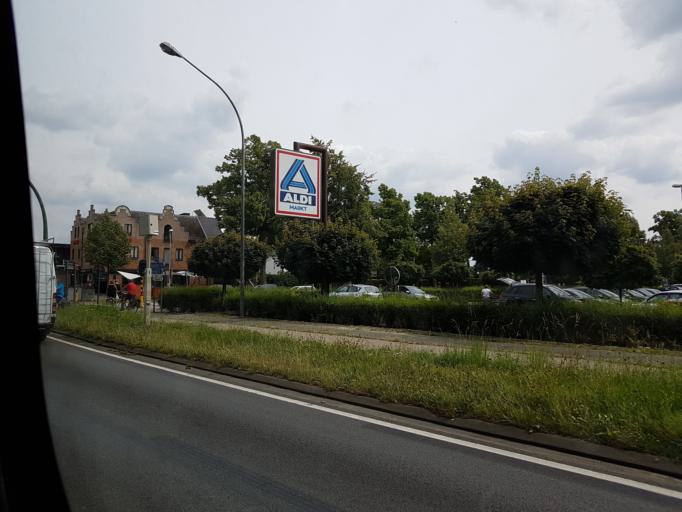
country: BE
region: Flanders
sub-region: Provincie Antwerpen
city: Westerlo
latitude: 51.0898
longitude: 4.9139
